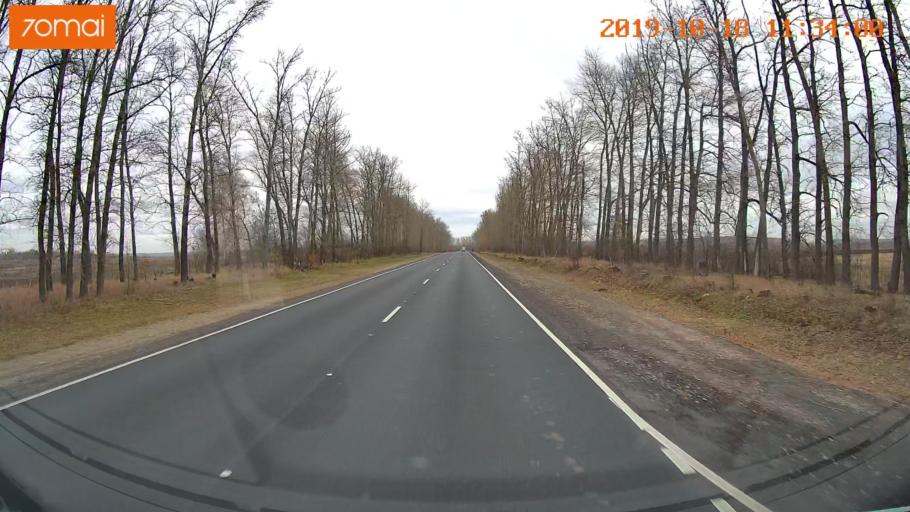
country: RU
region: Rjazan
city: Oktyabr'skiy
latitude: 54.1375
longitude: 38.7543
